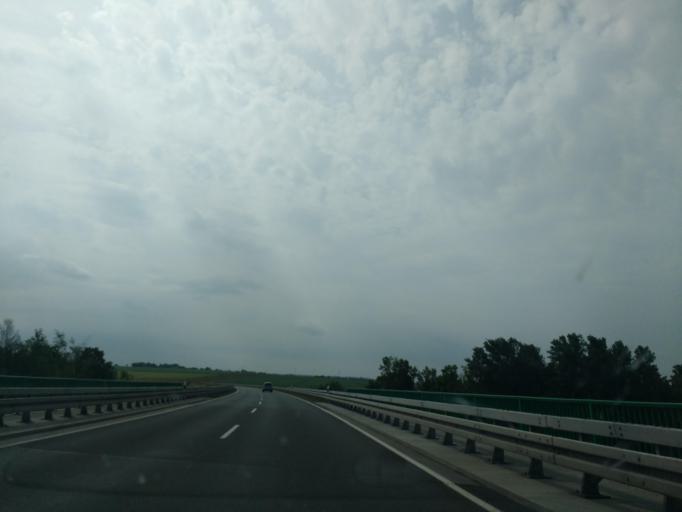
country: DE
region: Saxony-Anhalt
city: Theissen
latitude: 51.0922
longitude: 12.1137
